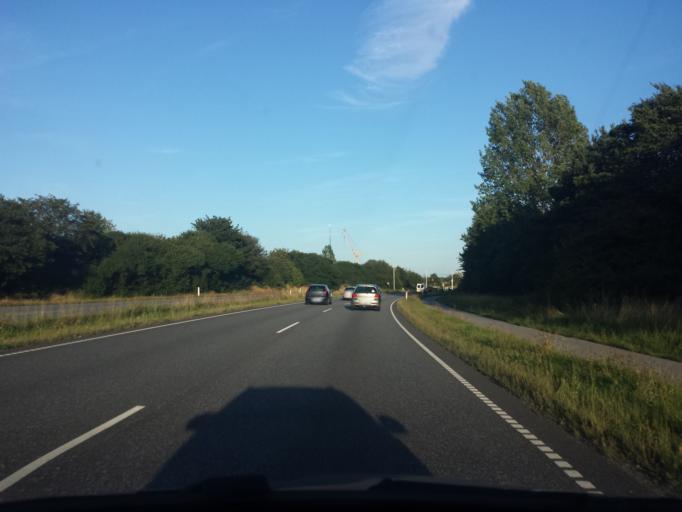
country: DK
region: Capital Region
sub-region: Egedal Kommune
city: Stenlose
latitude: 55.7793
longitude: 12.1790
